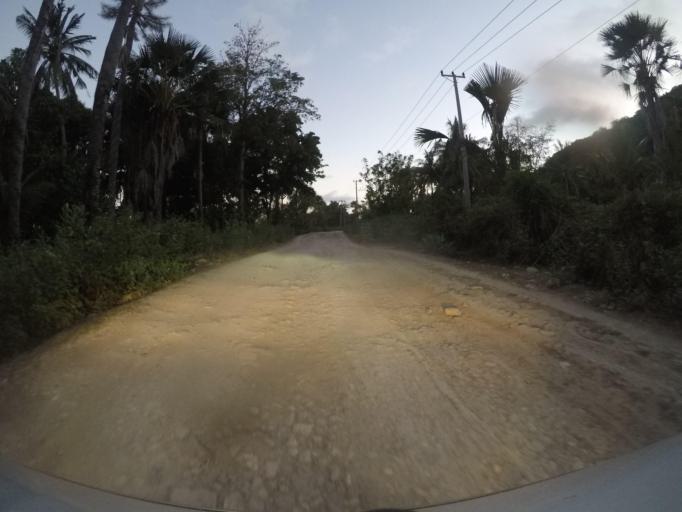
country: TL
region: Viqueque
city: Viqueque
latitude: -8.7948
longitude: 126.6238
